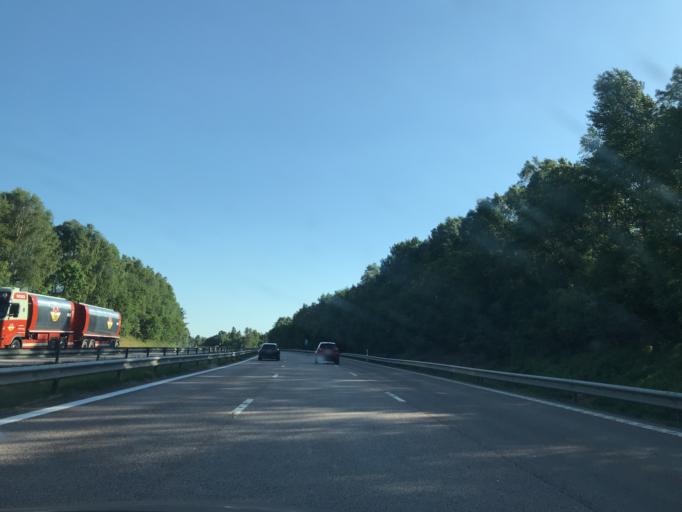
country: SE
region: Skane
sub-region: Bastads Kommun
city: Bastad
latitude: 56.3537
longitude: 12.9333
